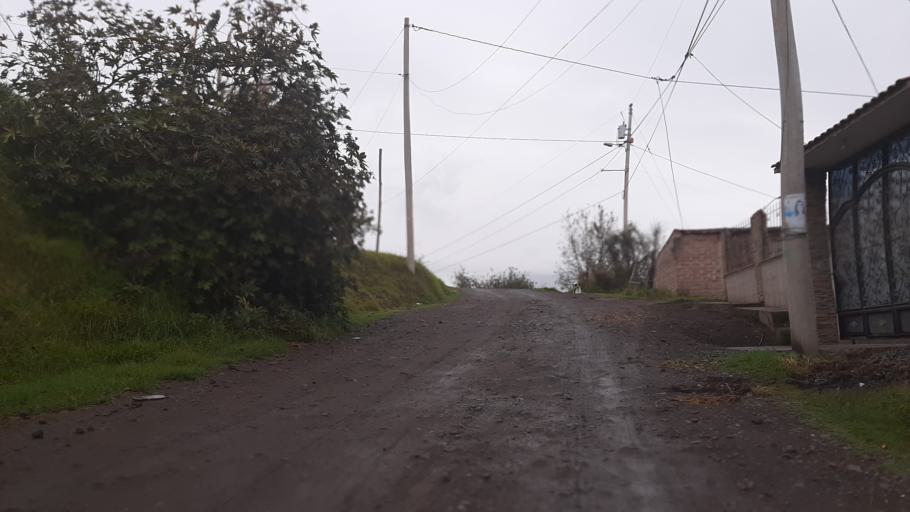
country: EC
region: Chimborazo
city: Riobamba
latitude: -1.6495
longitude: -78.6376
